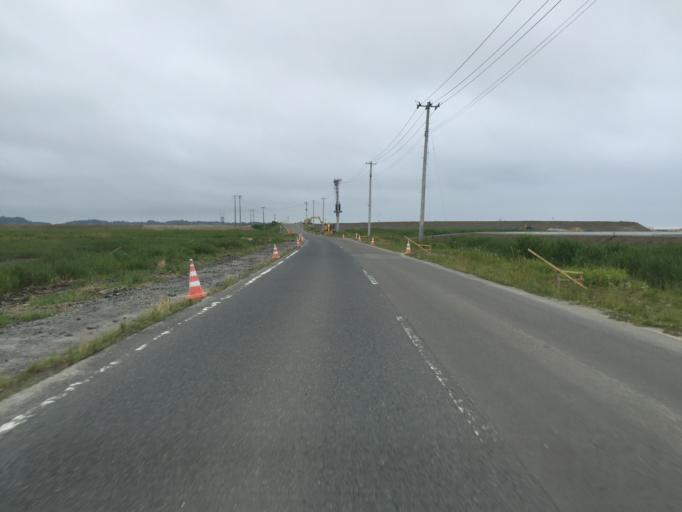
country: JP
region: Fukushima
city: Namie
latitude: 37.6835
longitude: 141.0047
